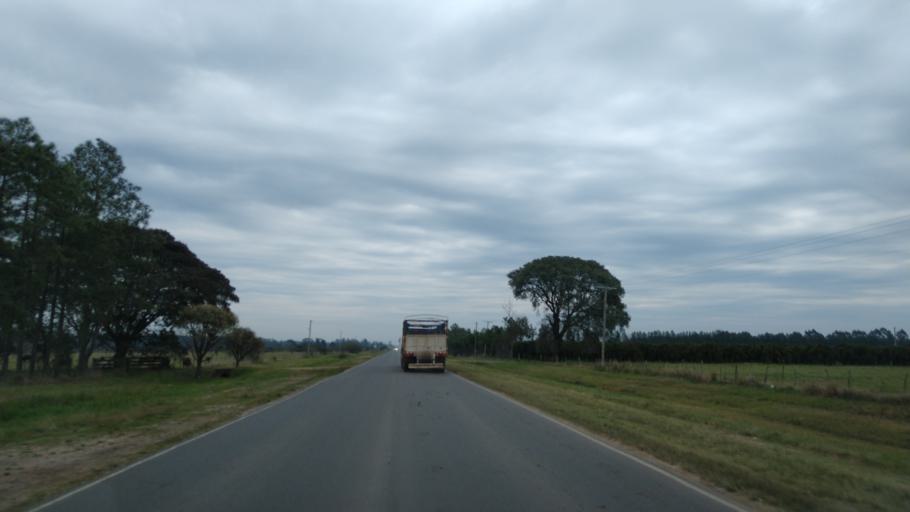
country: AR
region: Entre Rios
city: Villa del Rosario
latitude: -30.7923
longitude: -57.9412
